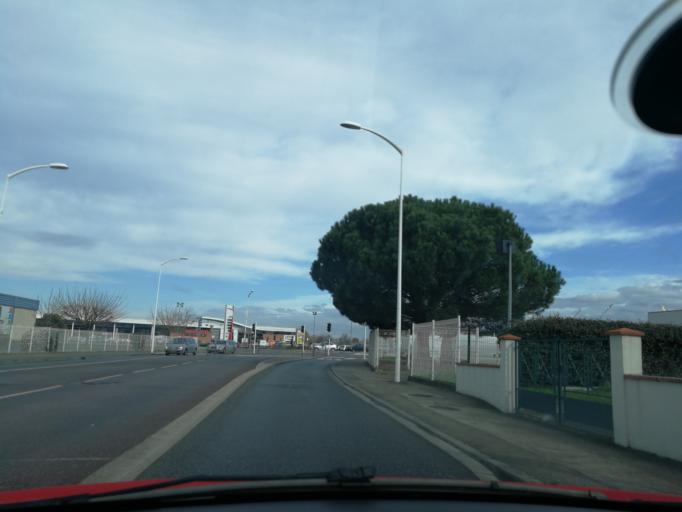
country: FR
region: Midi-Pyrenees
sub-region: Departement de la Haute-Garonne
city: Balma
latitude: 43.6132
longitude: 1.4888
